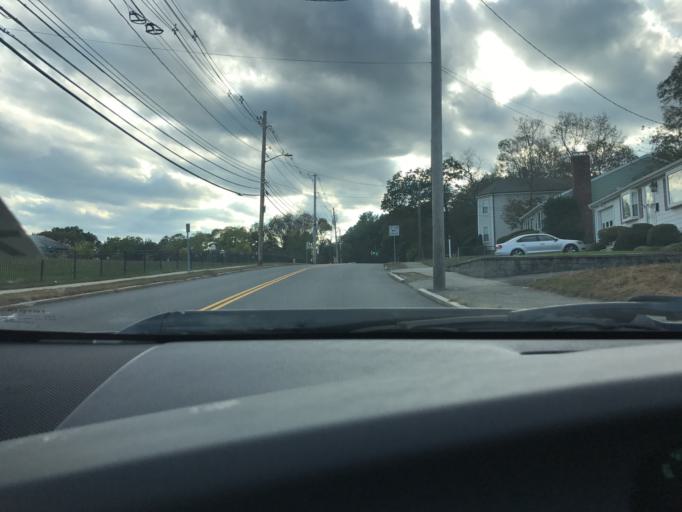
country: US
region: Massachusetts
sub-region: Middlesex County
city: Waltham
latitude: 42.3683
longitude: -71.2514
